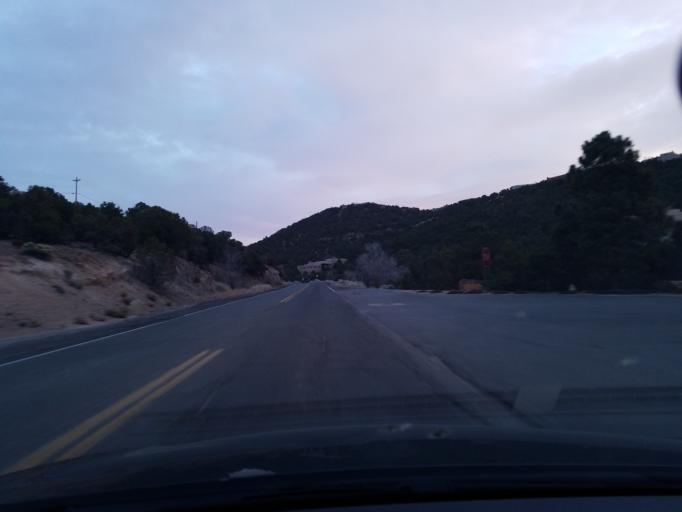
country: US
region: New Mexico
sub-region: Santa Fe County
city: Santa Fe
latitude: 35.6976
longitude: -105.9096
